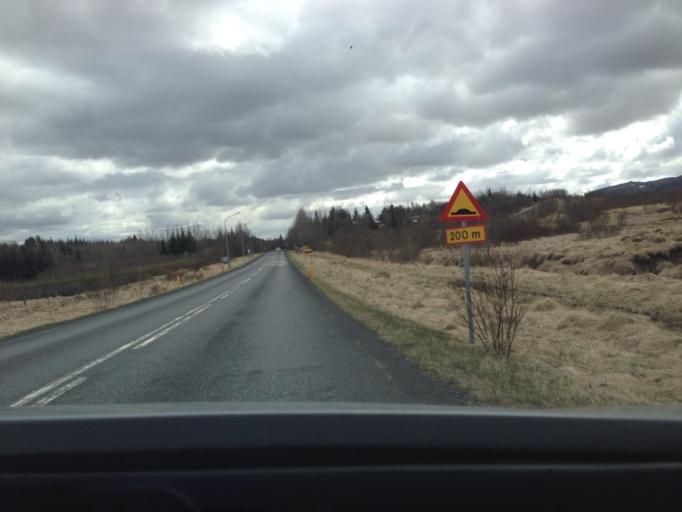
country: IS
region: South
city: Selfoss
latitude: 64.1210
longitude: -20.5040
